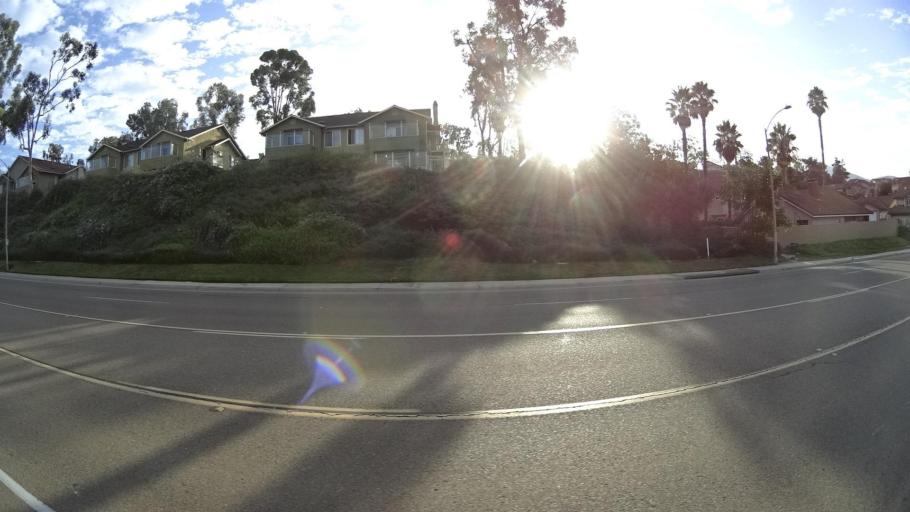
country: US
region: California
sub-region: San Diego County
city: Spring Valley
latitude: 32.7338
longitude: -116.9717
